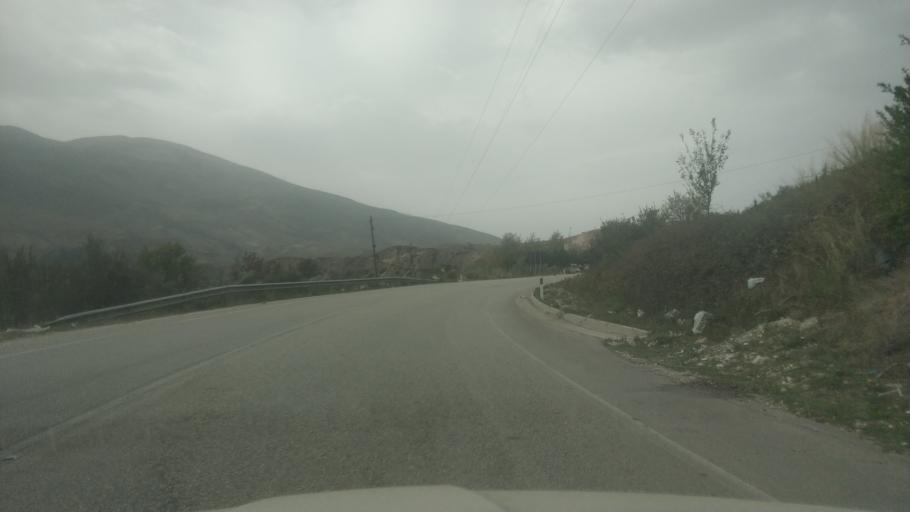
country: AL
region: Gjirokaster
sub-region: Rrethi i Tepelenes
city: Memaliaj
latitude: 40.3533
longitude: 19.9520
